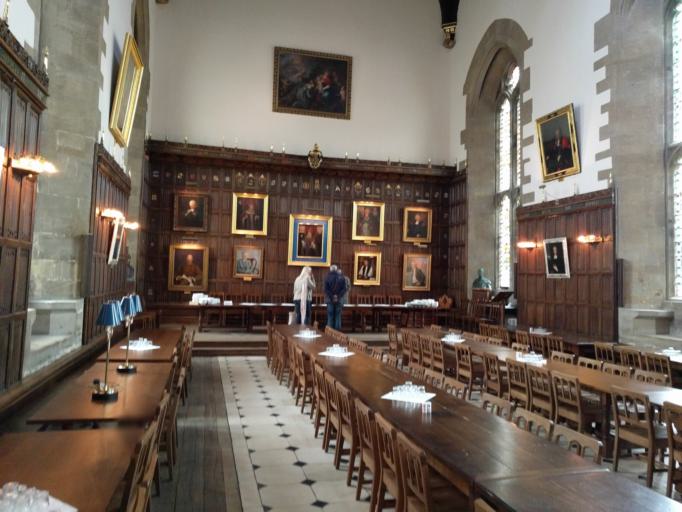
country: GB
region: England
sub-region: Oxfordshire
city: Oxford
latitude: 51.7542
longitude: -1.2517
